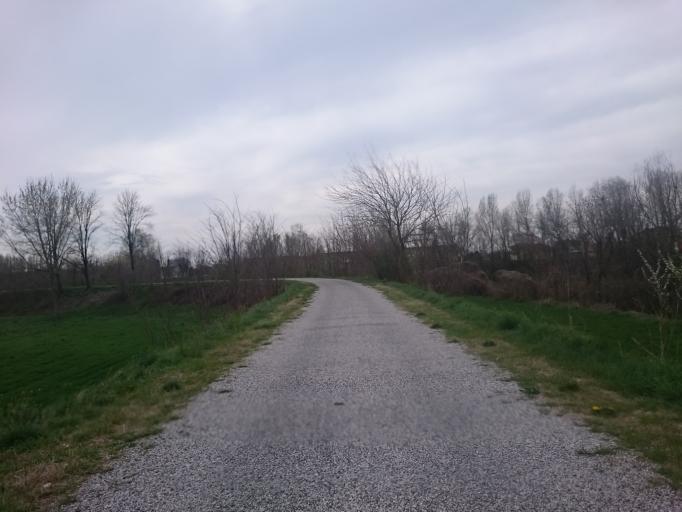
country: IT
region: Veneto
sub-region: Provincia di Padova
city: Limena
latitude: 45.4733
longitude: 11.8505
